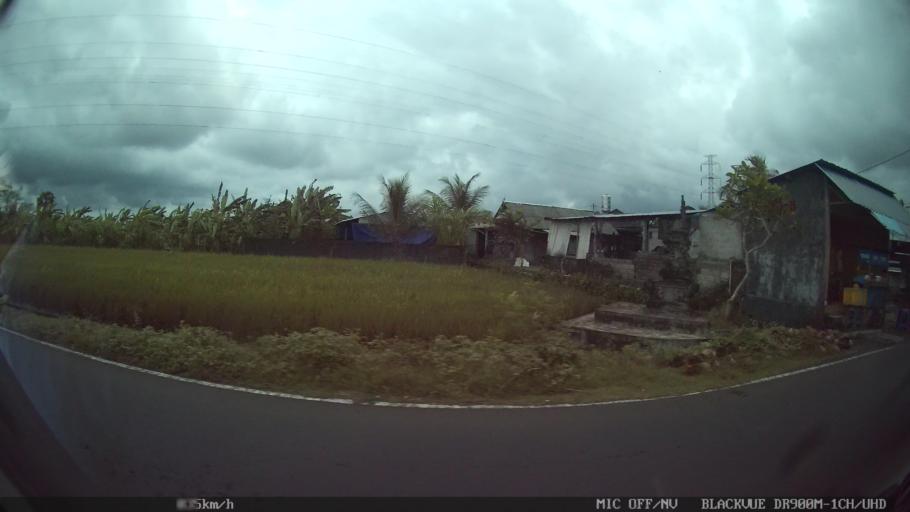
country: ID
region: Bali
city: Banjar Serangan
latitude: -8.5484
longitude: 115.1822
